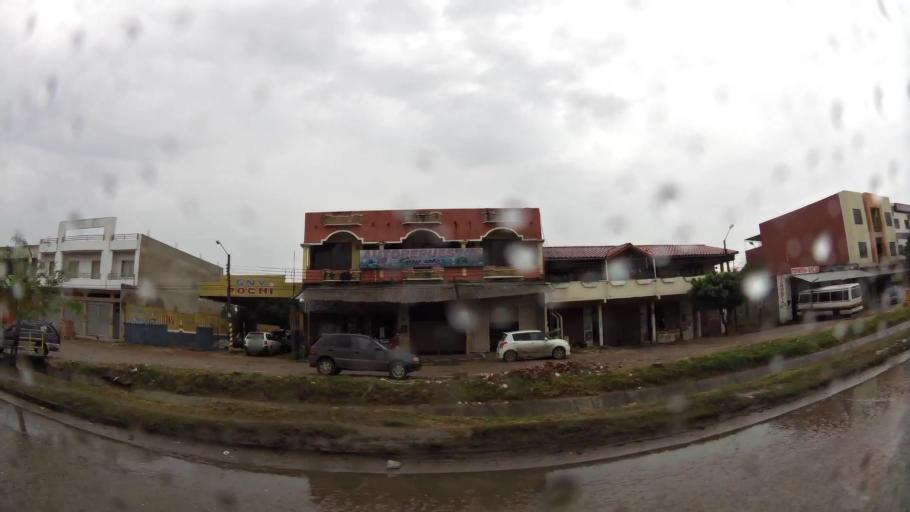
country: BO
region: Santa Cruz
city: Santa Cruz de la Sierra
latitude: -17.8111
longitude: -63.1286
